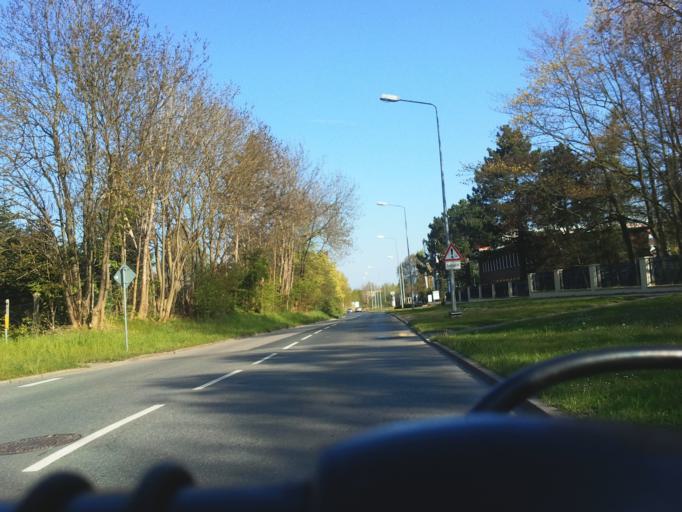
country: DE
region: Mecklenburg-Vorpommern
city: Rostock
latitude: 54.1017
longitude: 12.0936
